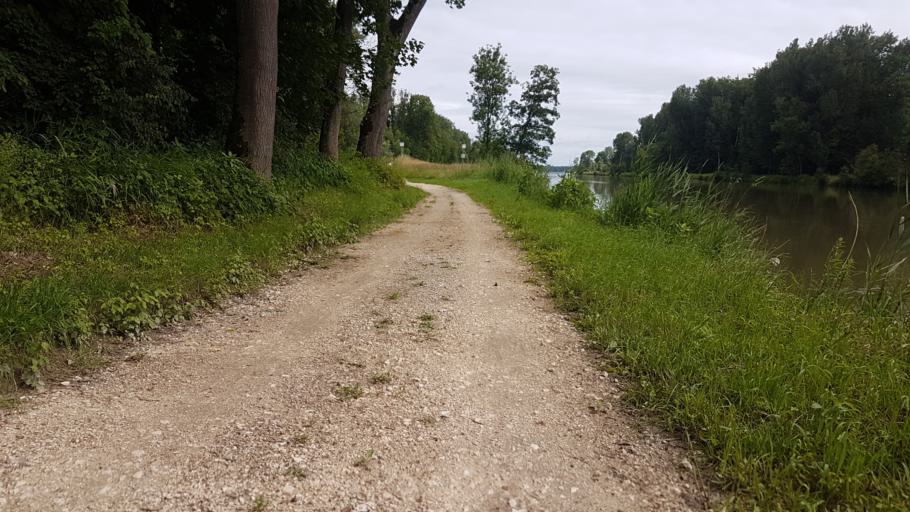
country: DE
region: Bavaria
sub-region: Swabia
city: Gundremmingen
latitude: 48.5262
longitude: 10.3879
